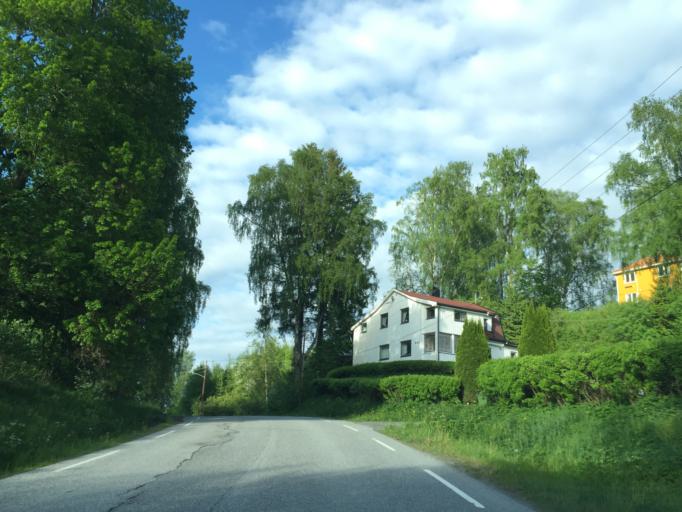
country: NO
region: Akershus
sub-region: Nes
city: Auli
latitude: 60.0060
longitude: 11.3044
